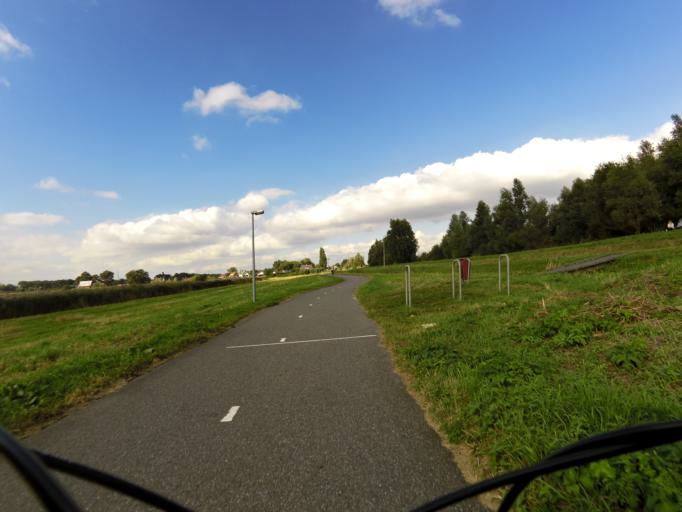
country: NL
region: South Holland
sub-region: Gemeente Voorschoten
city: Voorschoten
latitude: 52.1028
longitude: 4.4391
